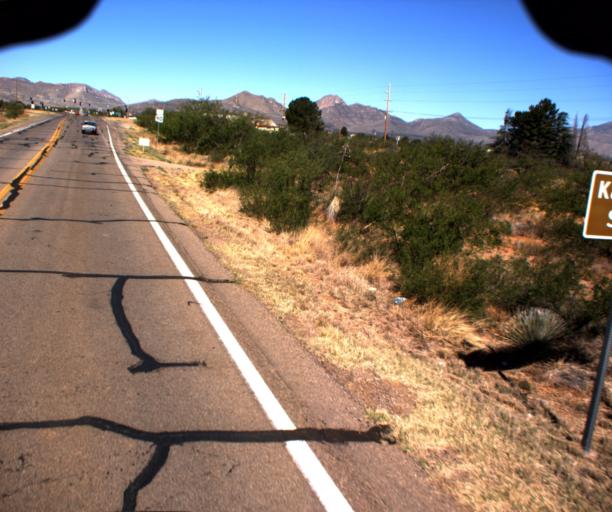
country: US
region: Arizona
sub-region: Cochise County
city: Huachuca City
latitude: 31.6929
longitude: -110.3466
